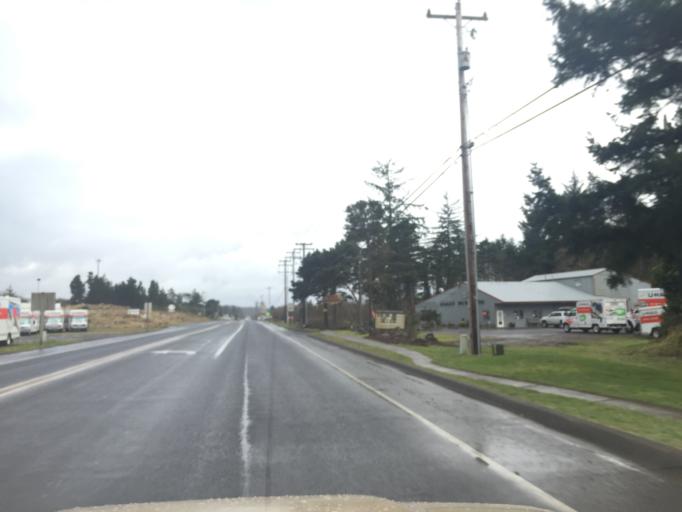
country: US
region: Oregon
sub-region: Lincoln County
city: Newport
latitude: 44.6103
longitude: -124.0515
